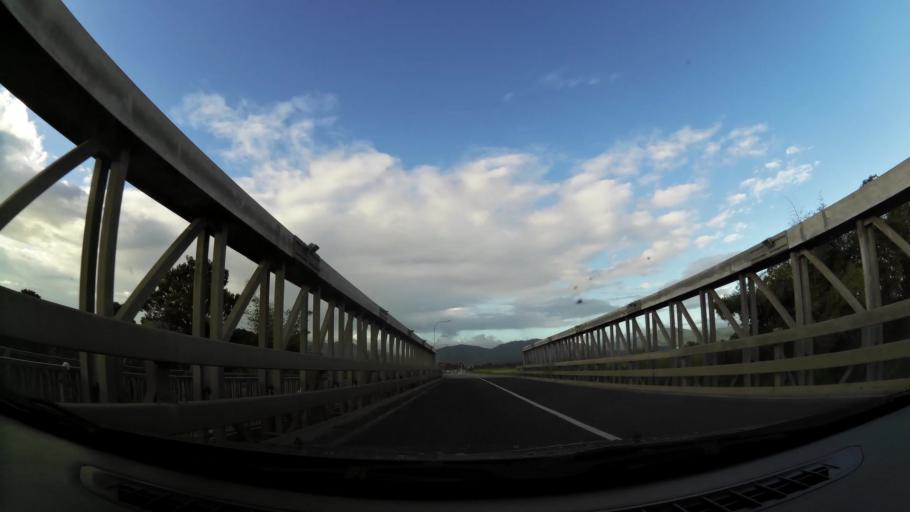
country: TT
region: Tunapuna/Piarco
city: Arouca
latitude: 10.5895
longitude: -61.3555
